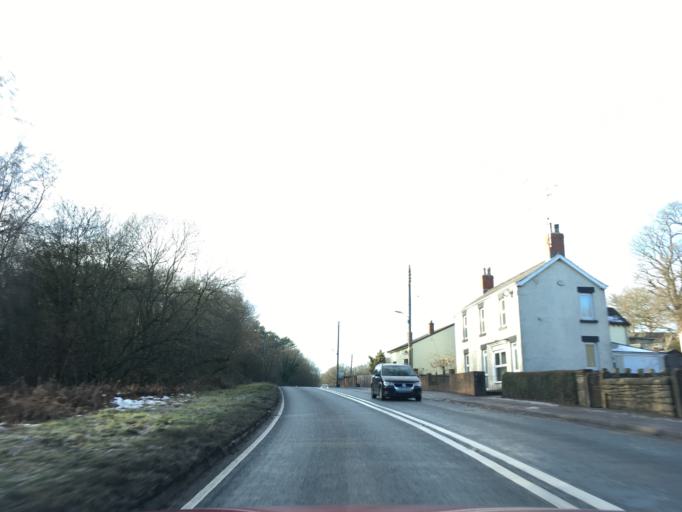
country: GB
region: England
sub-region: Gloucestershire
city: Ruardean
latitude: 51.8334
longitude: -2.5477
